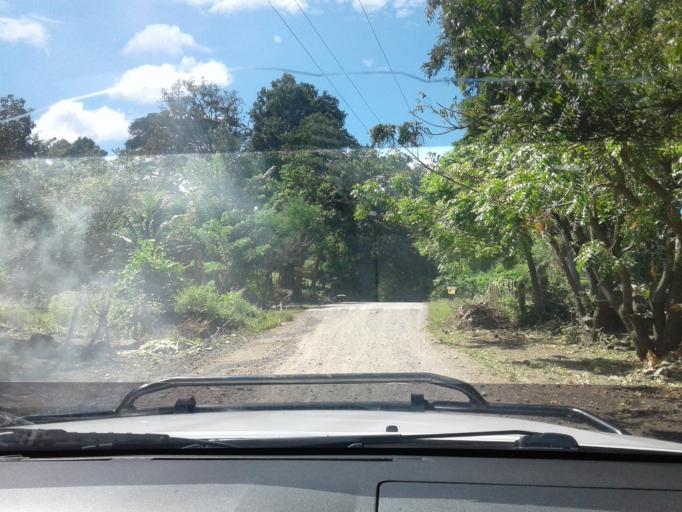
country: NI
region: Rivas
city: Altagracia
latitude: 11.4846
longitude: -85.5422
